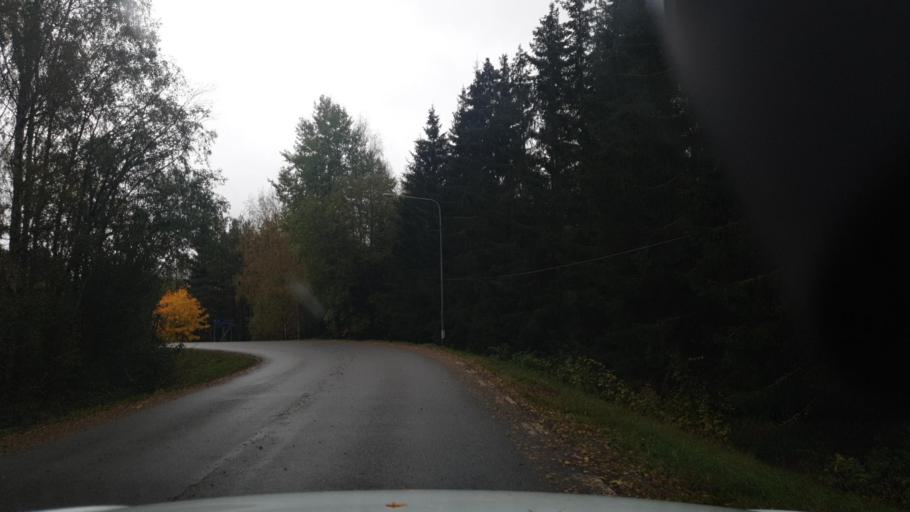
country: SE
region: Vaermland
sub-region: Karlstads Kommun
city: Valberg
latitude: 59.4081
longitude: 13.1813
